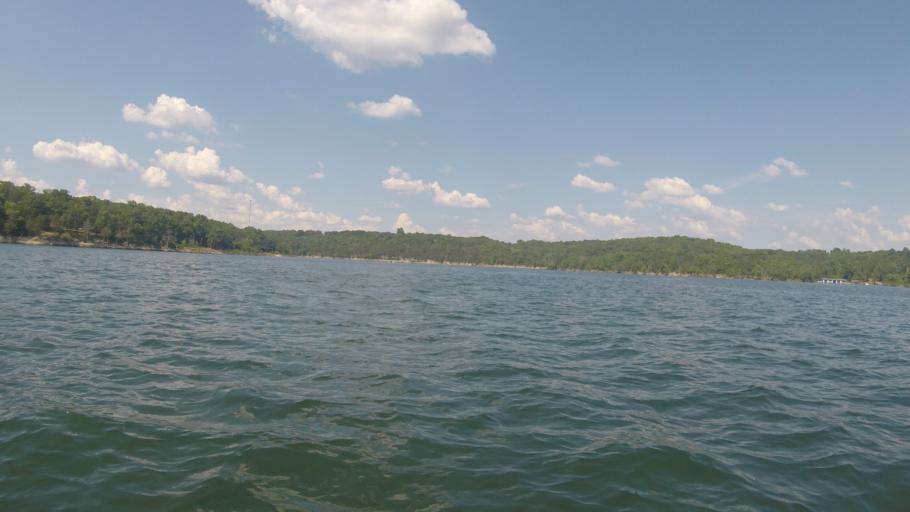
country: US
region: Missouri
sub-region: Barry County
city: Shell Knob
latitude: 36.5652
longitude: -93.5965
